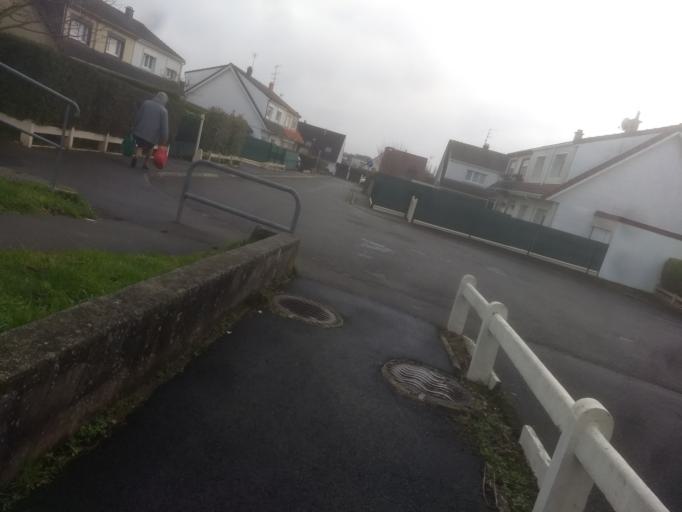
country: FR
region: Nord-Pas-de-Calais
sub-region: Departement du Pas-de-Calais
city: Saint-Nicolas
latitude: 50.3036
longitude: 2.7908
